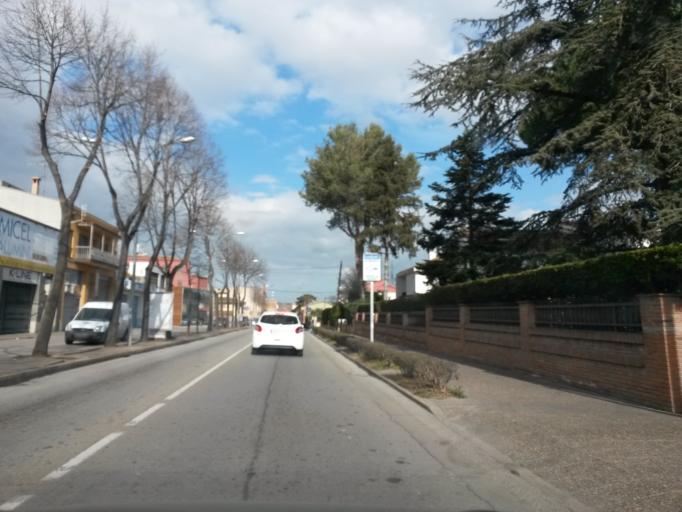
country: ES
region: Catalonia
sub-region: Provincia de Girona
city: Sarria de Ter
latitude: 42.0077
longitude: 2.8250
